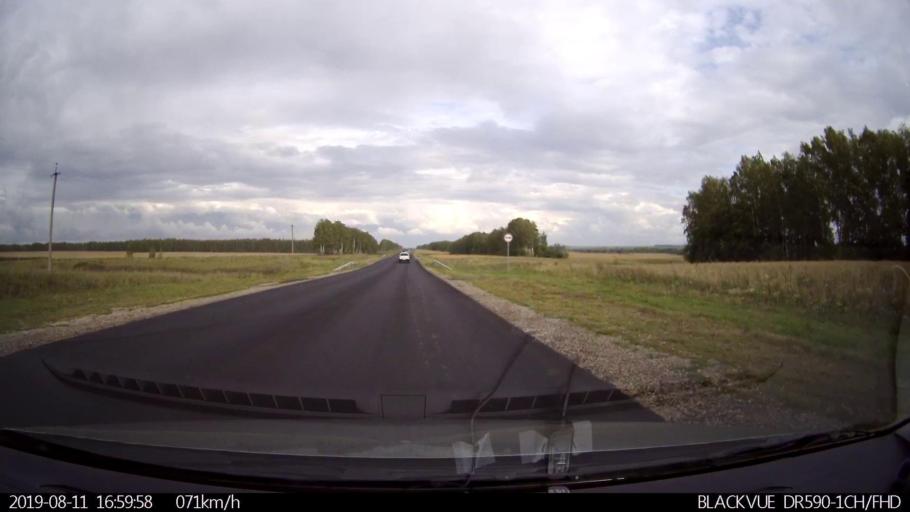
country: RU
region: Ulyanovsk
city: Mayna
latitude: 54.3114
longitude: 47.6713
